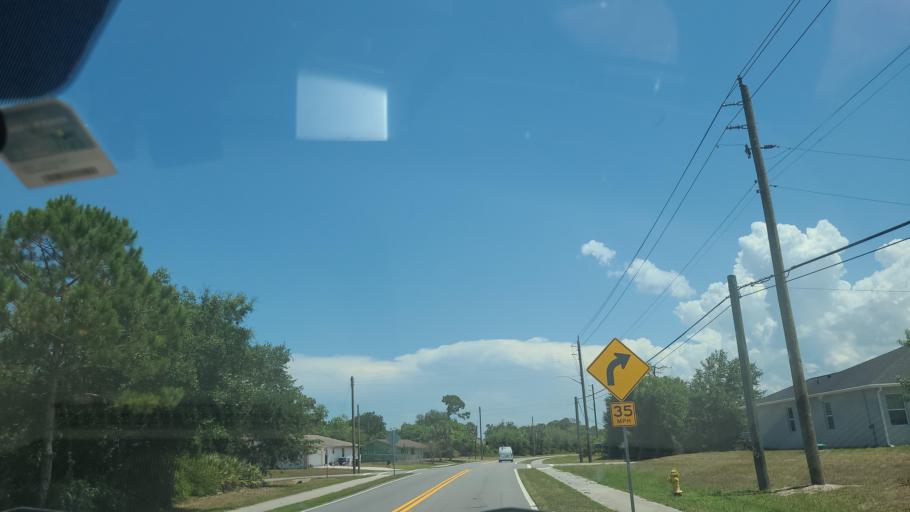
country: US
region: Florida
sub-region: Brevard County
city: Grant-Valkaria
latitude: 27.9515
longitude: -80.6277
